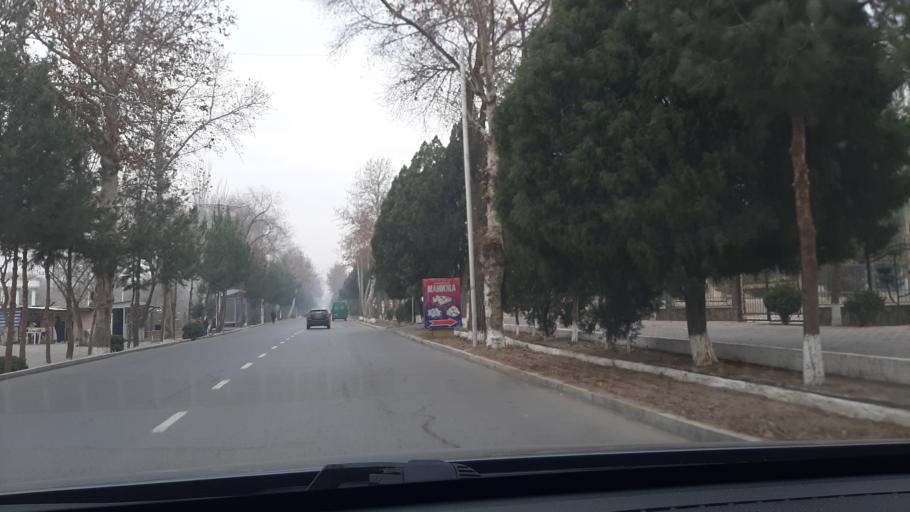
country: TJ
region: Viloyati Sughd
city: Palos
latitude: 40.2661
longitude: 69.7988
